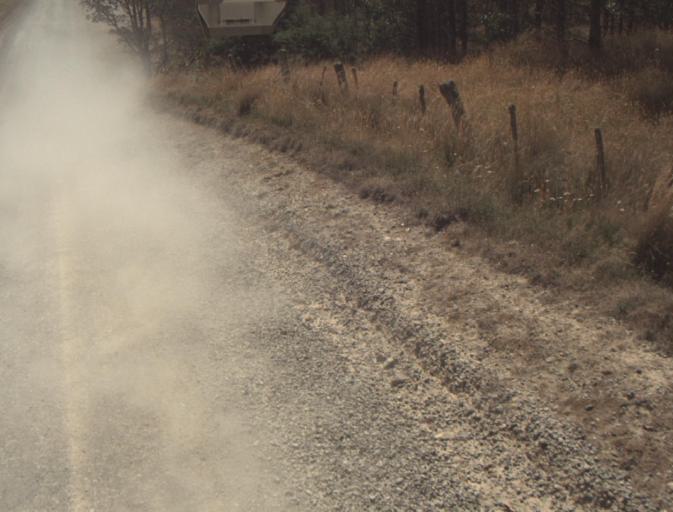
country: AU
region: Tasmania
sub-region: Dorset
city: Scottsdale
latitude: -41.3481
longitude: 147.4480
